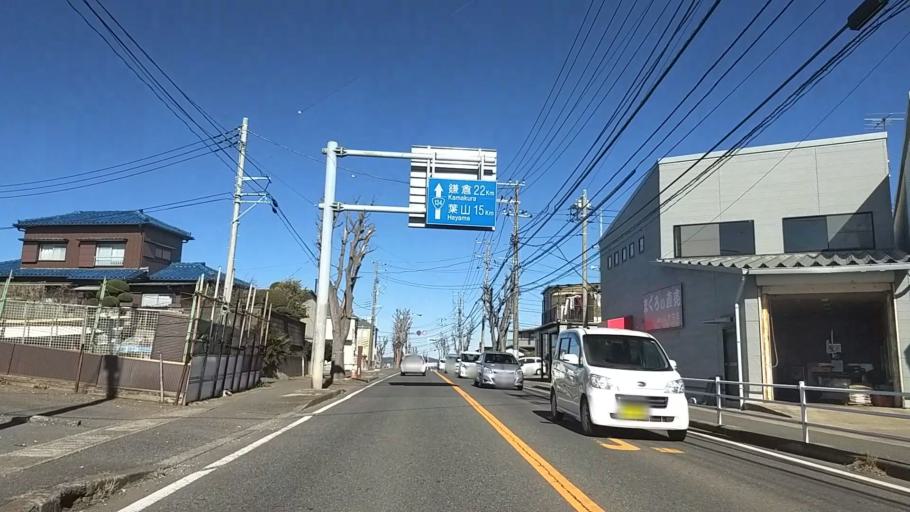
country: JP
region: Kanagawa
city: Miura
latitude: 35.1681
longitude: 139.6397
